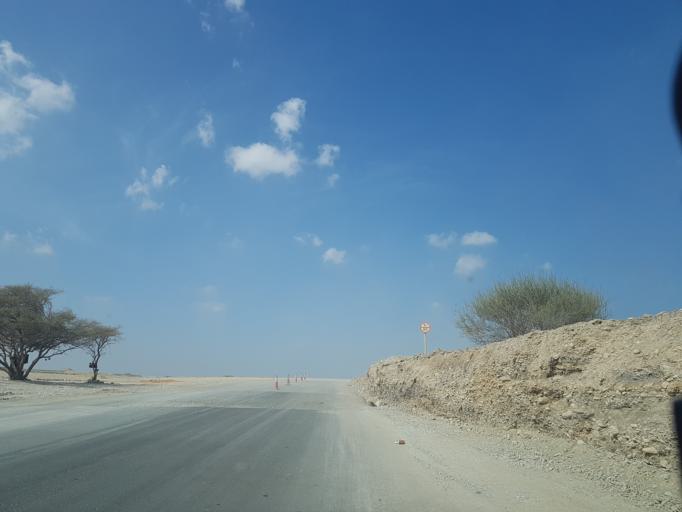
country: AE
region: Ra's al Khaymah
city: Ras al-Khaimah
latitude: 25.7468
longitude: 56.0151
